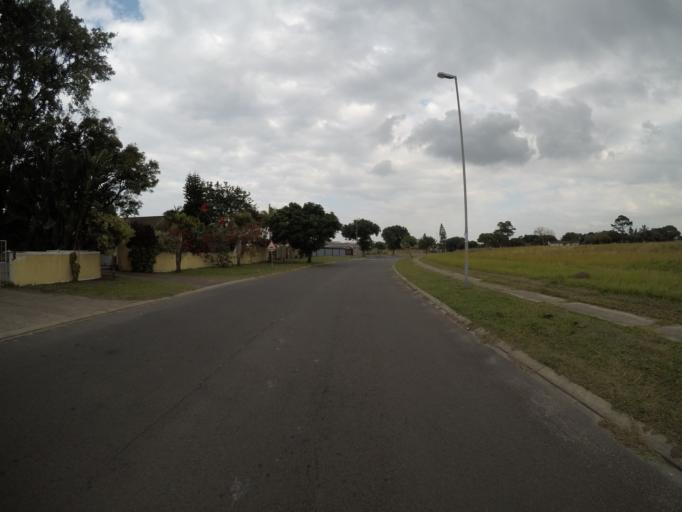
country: ZA
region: KwaZulu-Natal
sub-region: uThungulu District Municipality
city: Richards Bay
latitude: -28.7351
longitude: 32.0498
